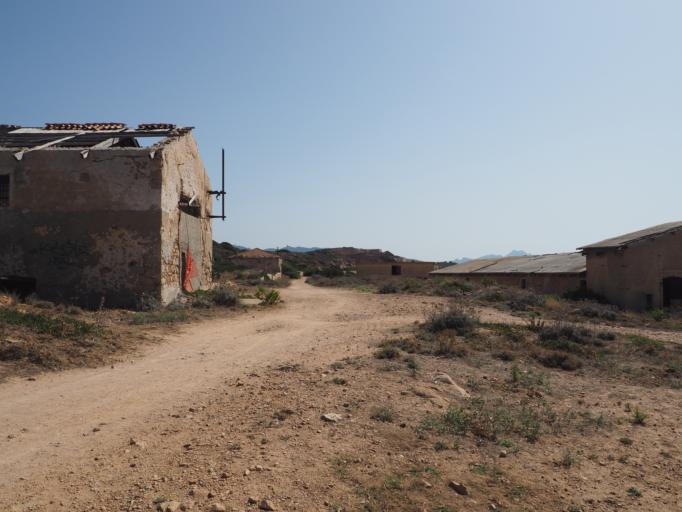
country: IT
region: Sardinia
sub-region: Provincia di Olbia-Tempio
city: La Maddalena
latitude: 41.1758
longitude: 9.4690
